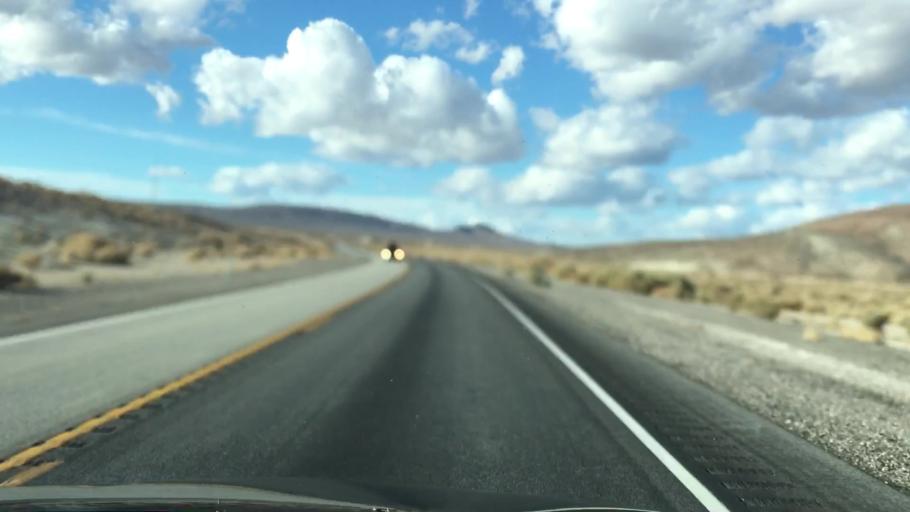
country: US
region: Nevada
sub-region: Nye County
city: Beatty
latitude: 37.0347
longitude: -116.7599
